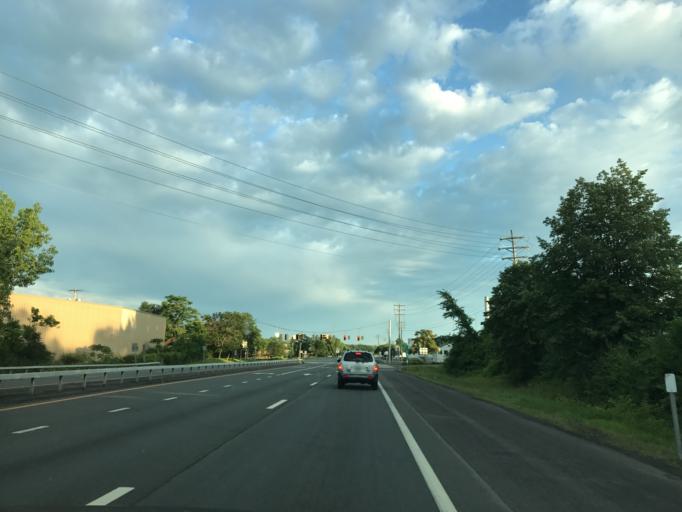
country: US
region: New York
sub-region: Albany County
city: Cohoes
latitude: 42.7627
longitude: -73.6987
